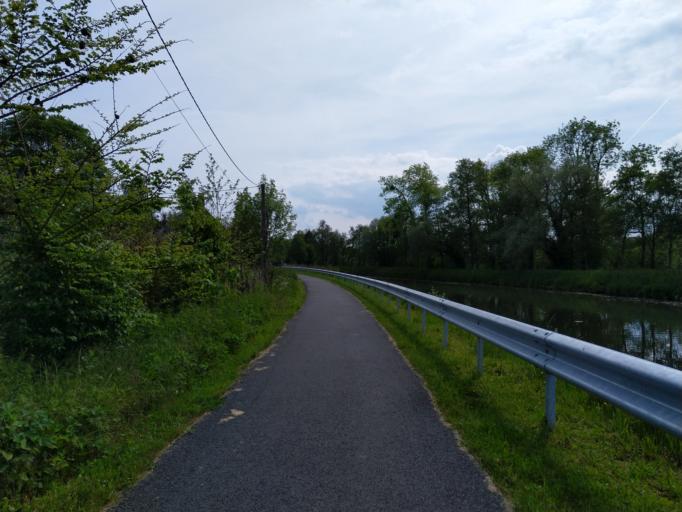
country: FR
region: Picardie
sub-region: Departement de l'Aisne
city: Etreux
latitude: 49.9737
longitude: 3.6292
